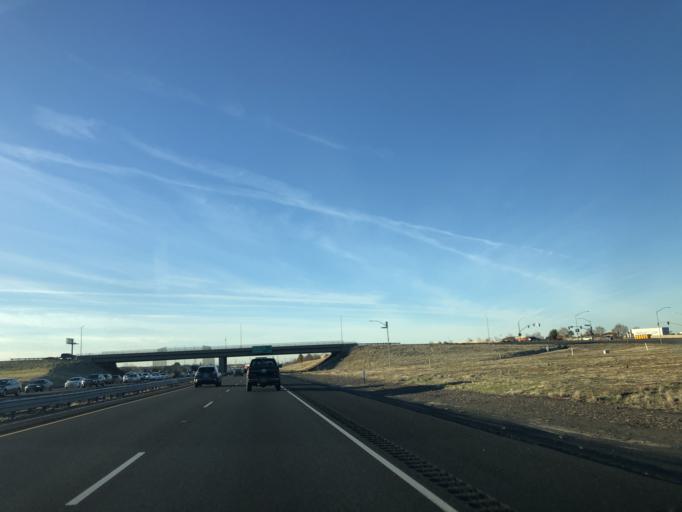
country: US
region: California
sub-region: Placer County
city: Roseville
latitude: 38.7855
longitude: -121.2818
